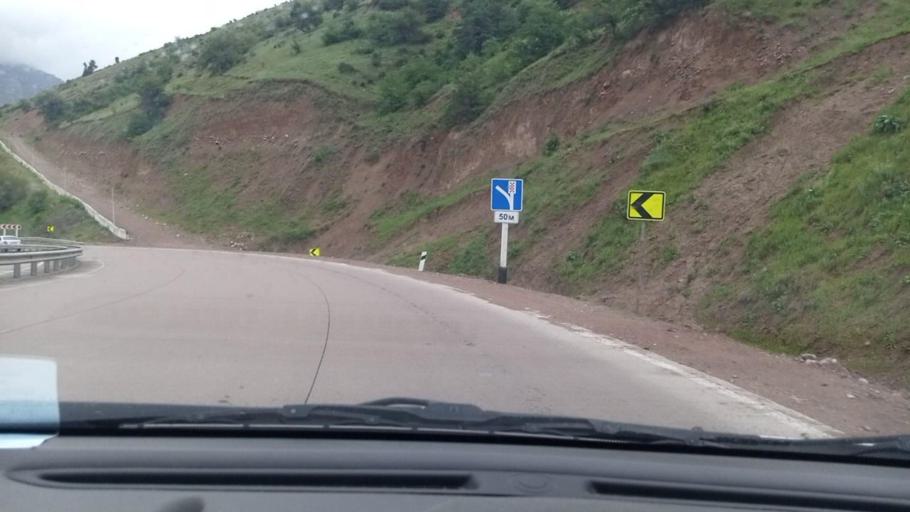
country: UZ
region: Toshkent
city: Angren
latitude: 41.1538
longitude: 70.4476
